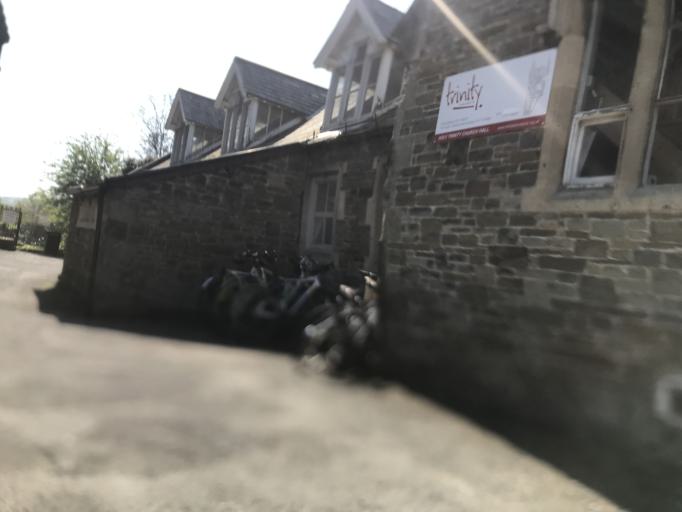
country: GB
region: England
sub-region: Devon
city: Barnstaple
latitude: 51.0762
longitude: -4.0544
